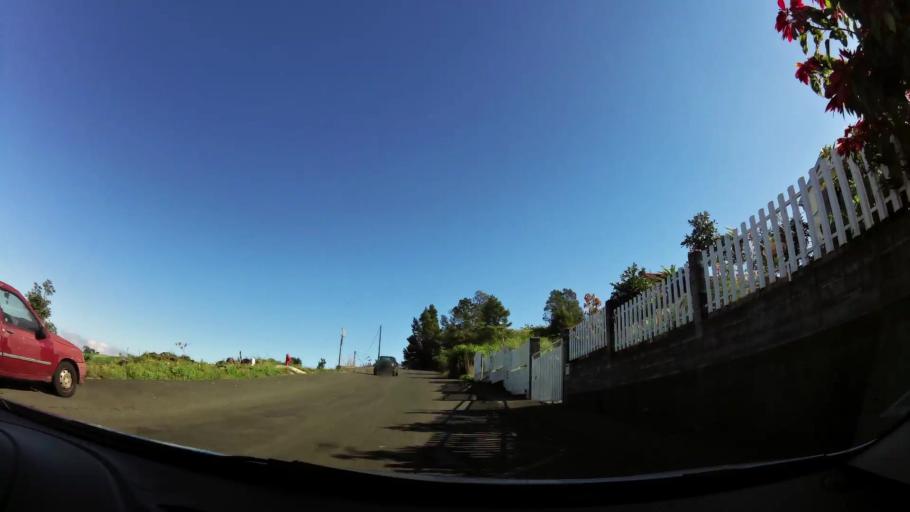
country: RE
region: Reunion
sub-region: Reunion
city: Le Tampon
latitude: -21.2358
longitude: 55.5238
